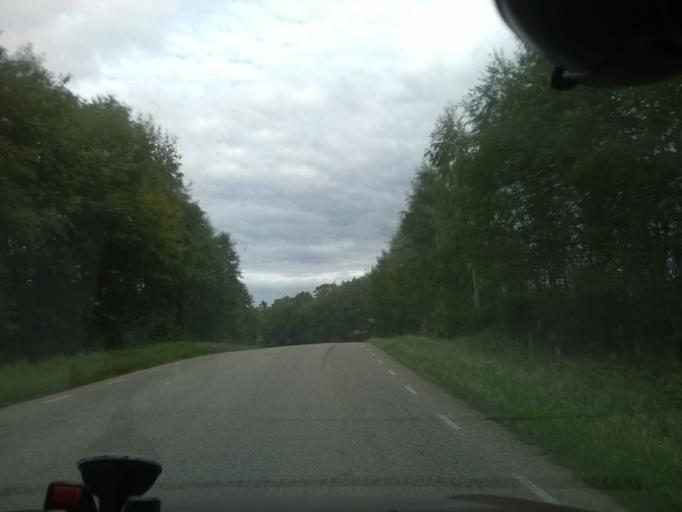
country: EE
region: Vorumaa
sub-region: Voru linn
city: Voru
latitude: 57.7666
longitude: 27.0155
